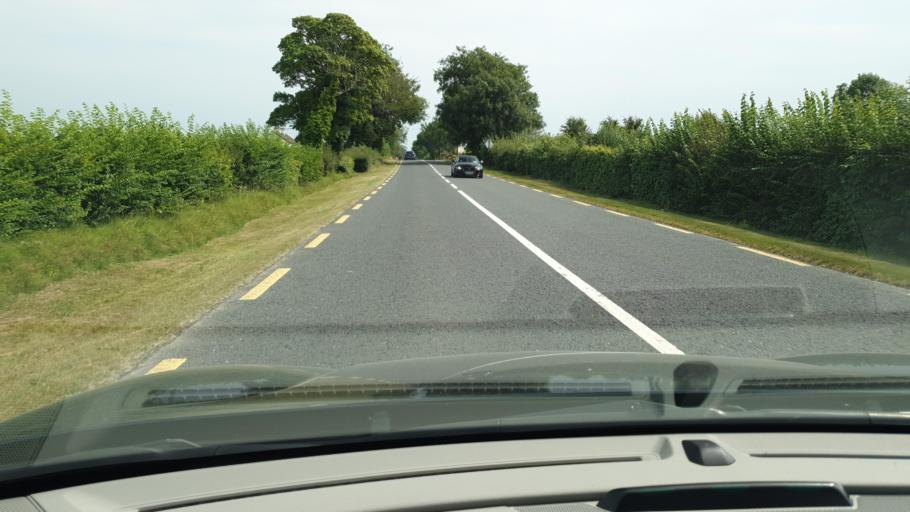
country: IE
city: Kentstown
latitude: 53.6332
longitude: -6.5659
